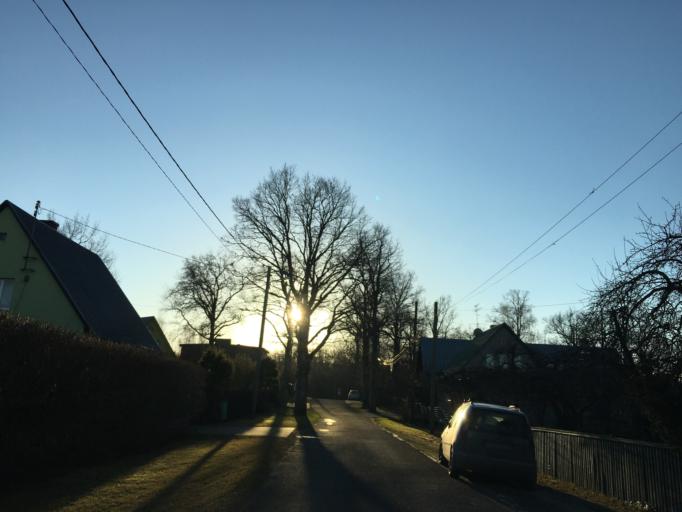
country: EE
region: Harju
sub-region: Saue linn
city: Saue
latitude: 59.3205
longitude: 24.5520
